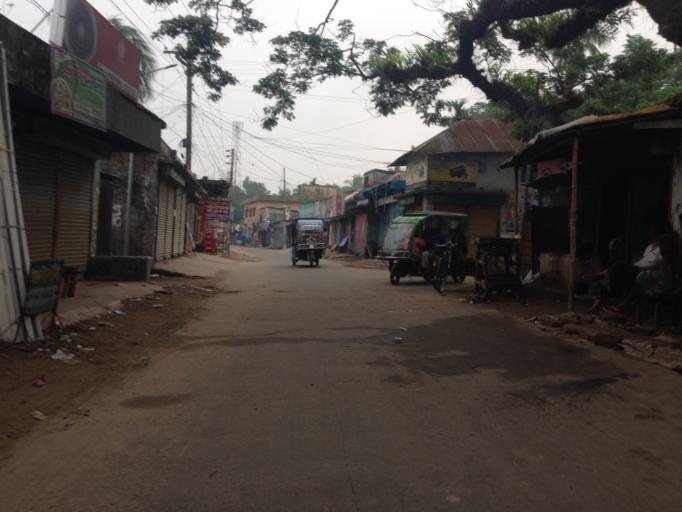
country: BD
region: Khulna
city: Kalia
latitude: 23.0391
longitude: 89.6323
